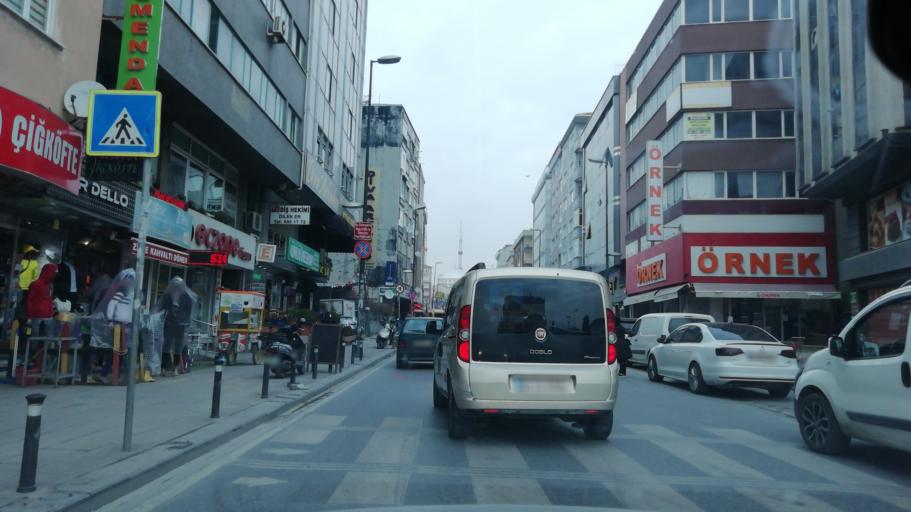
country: TR
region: Istanbul
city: Bahcelievler
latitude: 41.0146
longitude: 28.8419
